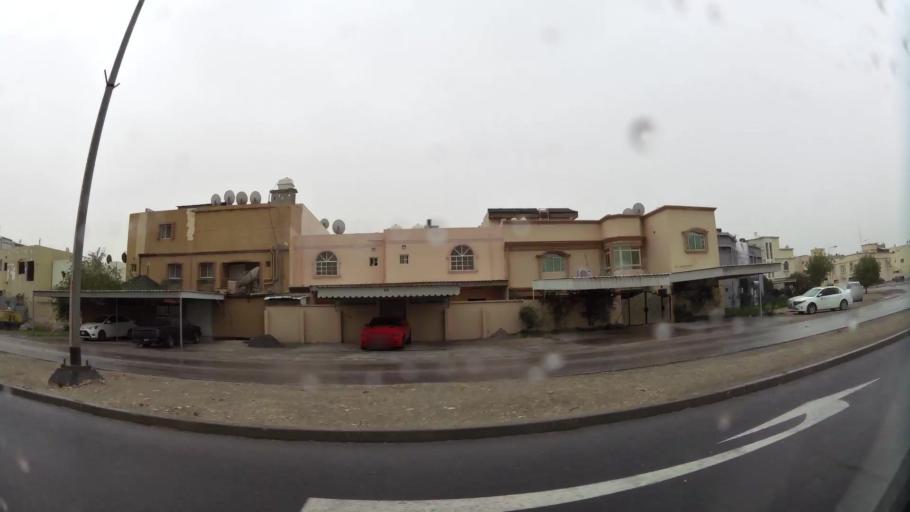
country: BH
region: Northern
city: Madinat `Isa
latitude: 26.1591
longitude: 50.5711
